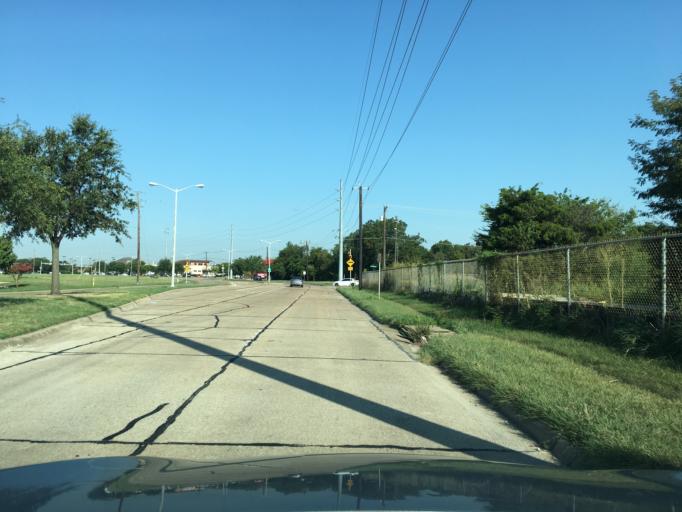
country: US
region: Texas
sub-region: Dallas County
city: Garland
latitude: 32.9583
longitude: -96.6616
